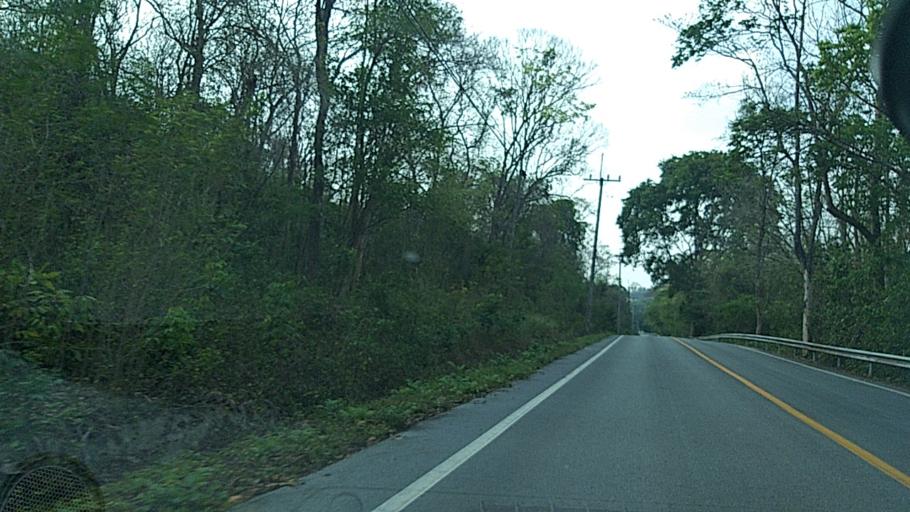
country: TH
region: Sara Buri
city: Saraburi
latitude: 14.4505
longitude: 100.9541
